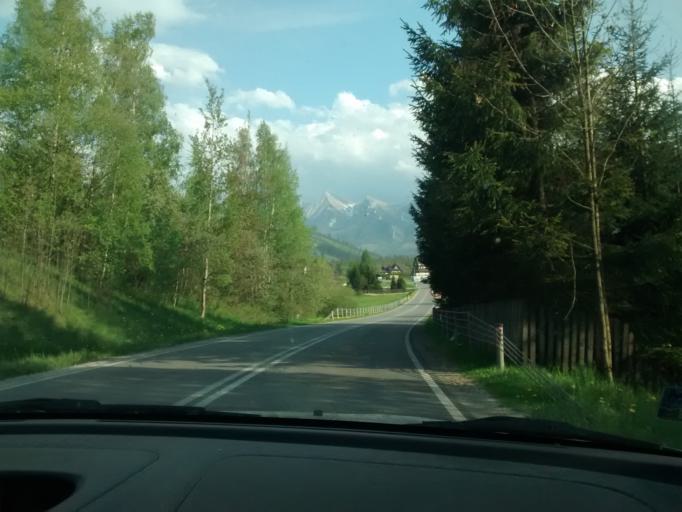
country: PL
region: Lesser Poland Voivodeship
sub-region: Powiat tatrzanski
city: Bukowina Tatrzanska
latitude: 49.3363
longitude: 20.1458
